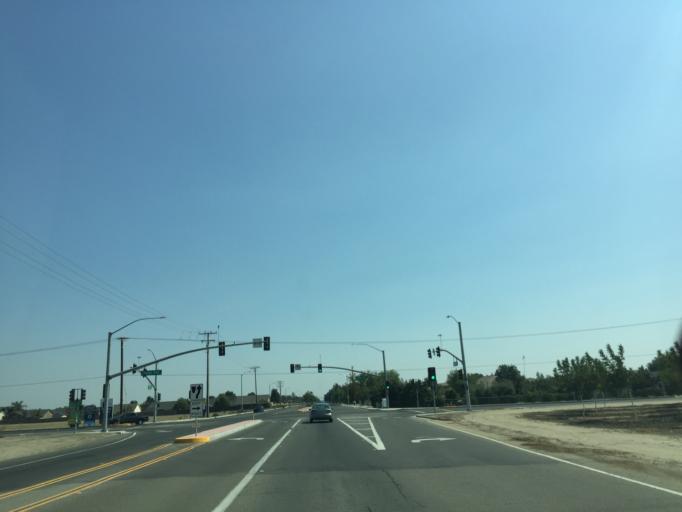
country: US
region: California
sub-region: Kings County
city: Lucerne
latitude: 36.3581
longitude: -119.6729
